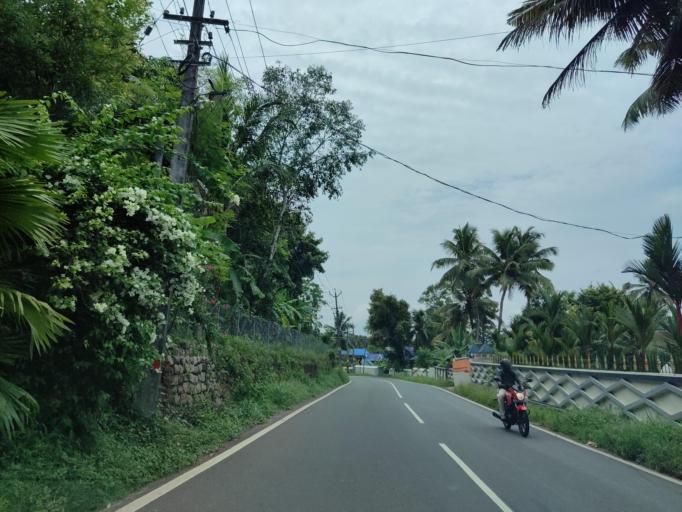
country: IN
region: Kerala
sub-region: Alappuzha
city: Chengannur
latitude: 9.2786
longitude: 76.6157
